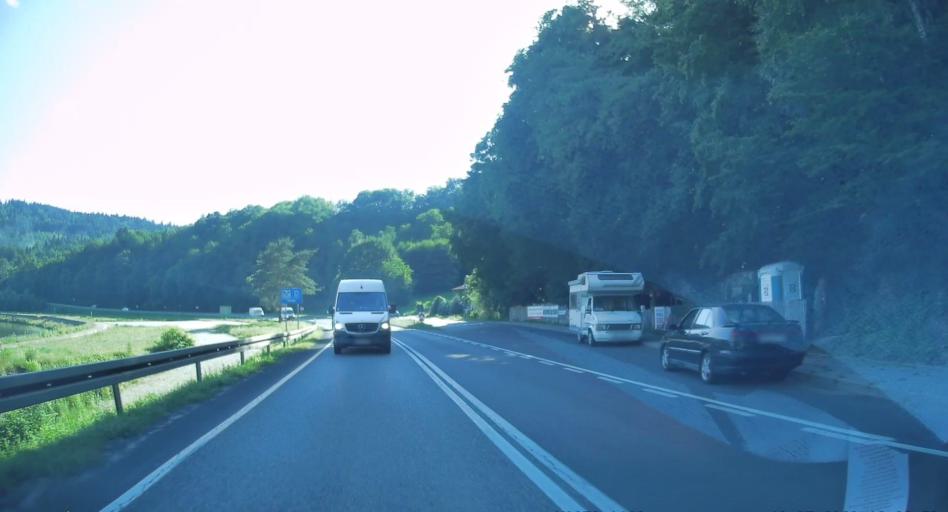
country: PL
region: Lesser Poland Voivodeship
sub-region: Powiat brzeski
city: Czchow
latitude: 49.8003
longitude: 20.6467
